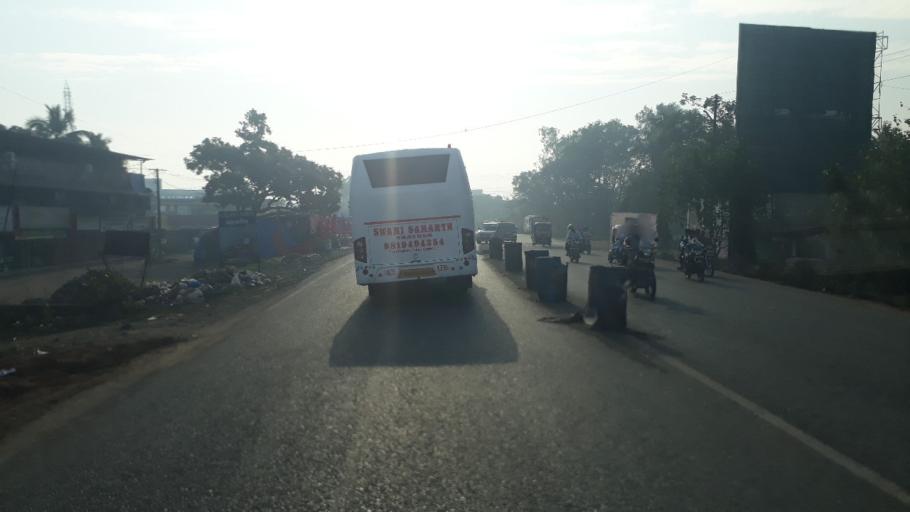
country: IN
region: Maharashtra
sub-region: Raigarh
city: Kalundri
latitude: 18.9724
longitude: 73.1296
